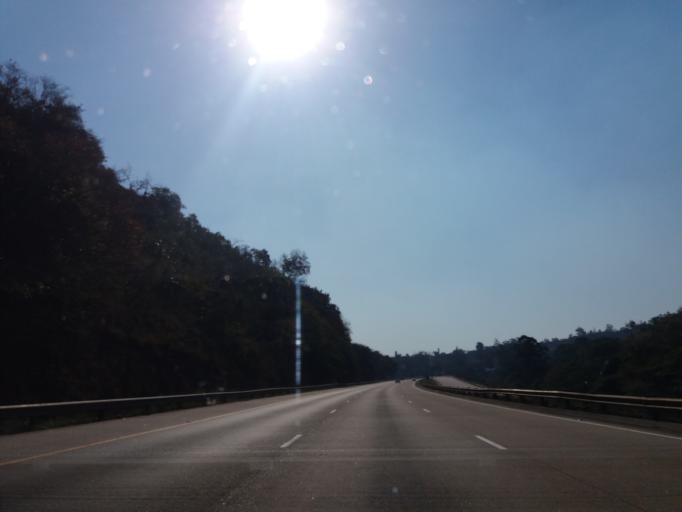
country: ZA
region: KwaZulu-Natal
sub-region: eThekwini Metropolitan Municipality
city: Mpumalanga
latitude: -29.7494
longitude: 30.6643
